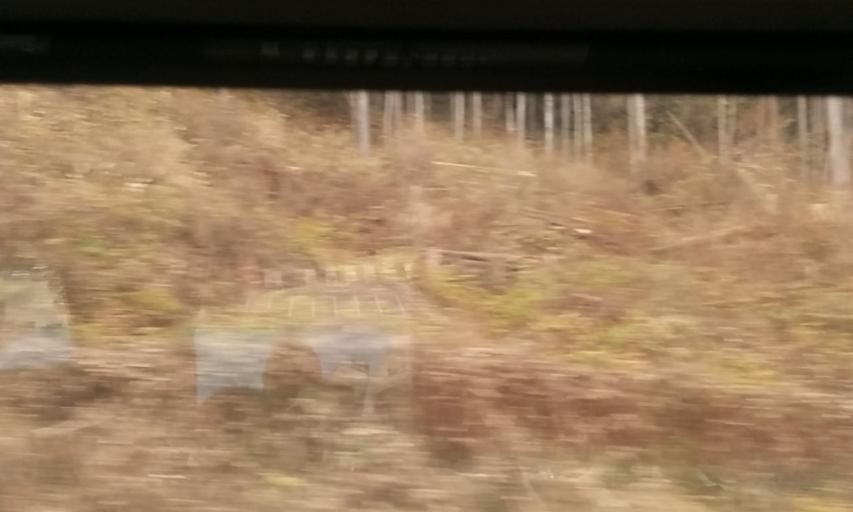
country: JP
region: Nagano
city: Iida
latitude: 35.7354
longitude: 137.7172
